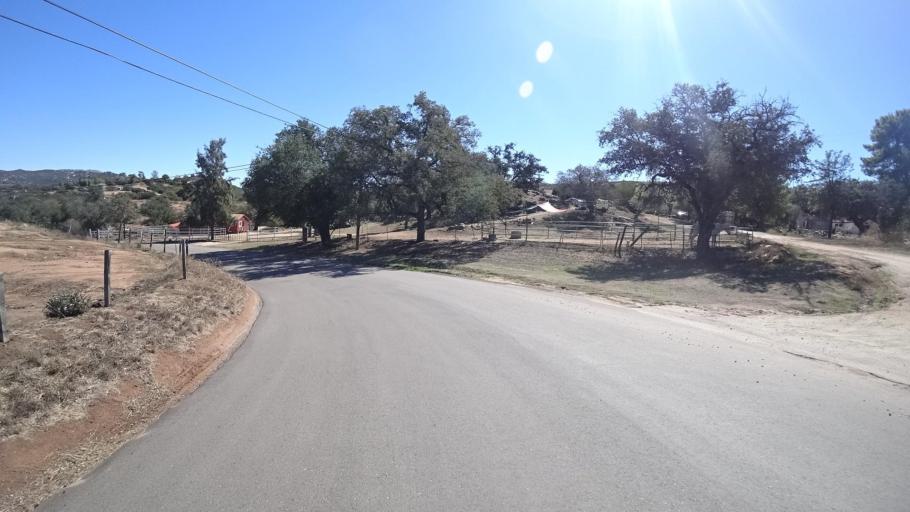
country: US
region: California
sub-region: San Diego County
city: Alpine
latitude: 32.7646
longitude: -116.6951
